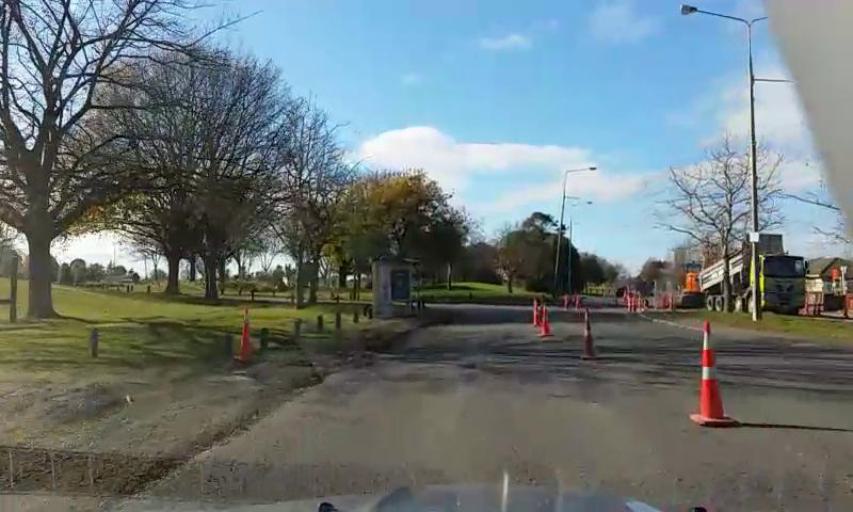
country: NZ
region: Canterbury
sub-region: Christchurch City
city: Christchurch
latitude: -43.4935
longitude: 172.7049
